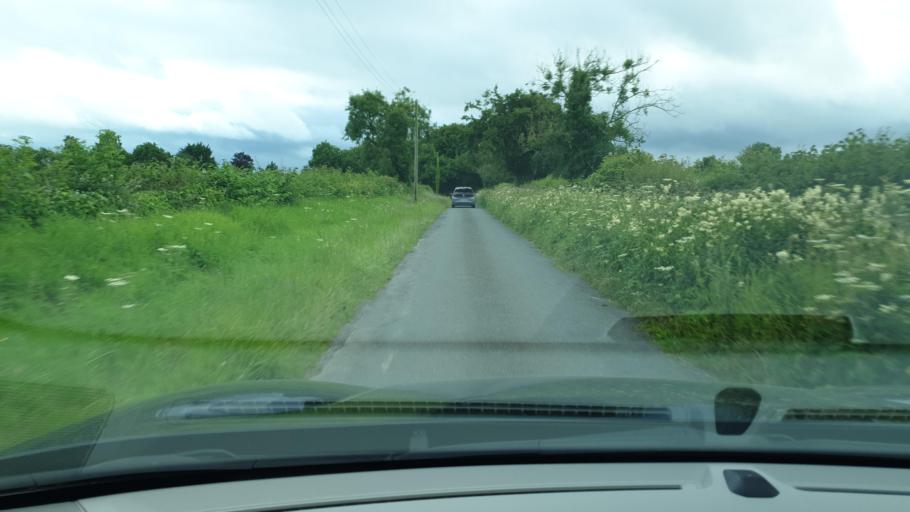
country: IE
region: Leinster
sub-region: An Mhi
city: Dunshaughlin
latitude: 53.5365
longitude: -6.5225
